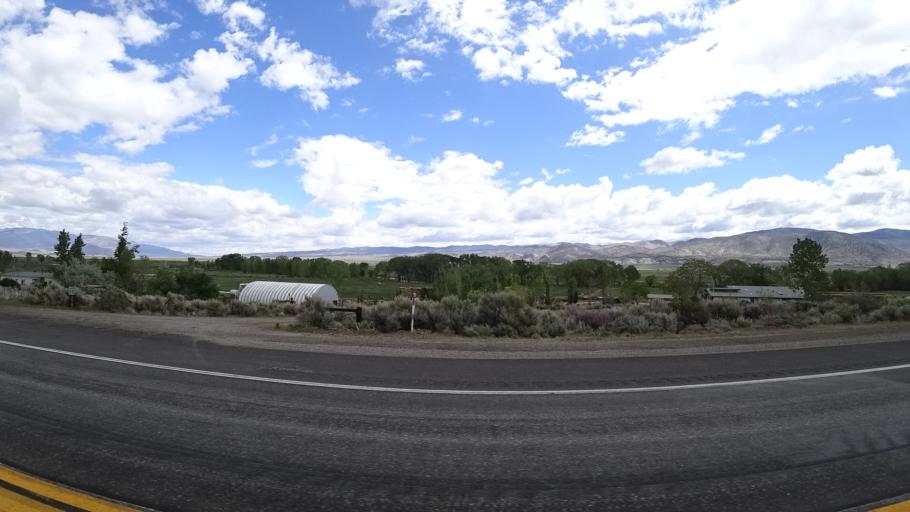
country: US
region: Nevada
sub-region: Lyon County
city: Smith Valley
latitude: 38.5860
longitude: -119.5139
